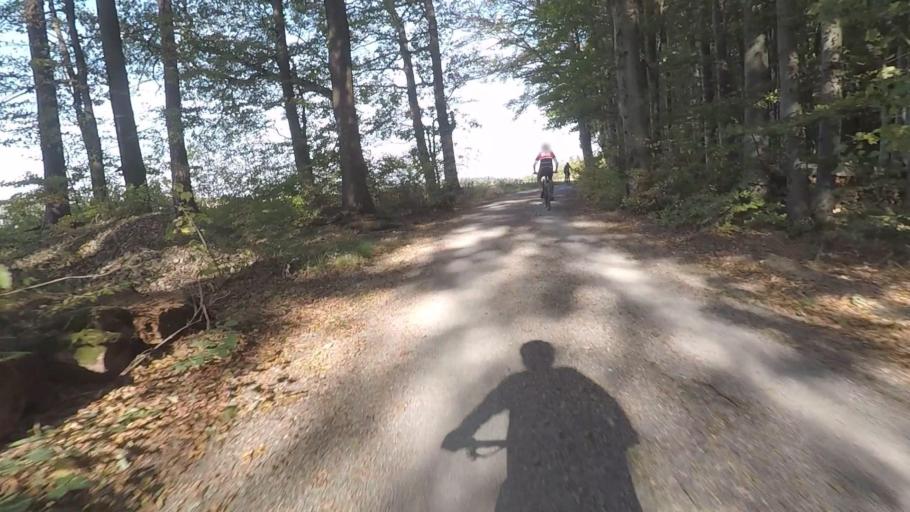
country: DE
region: Baden-Wuerttemberg
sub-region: Regierungsbezirk Stuttgart
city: Wustenrot
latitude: 49.0633
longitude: 9.4805
